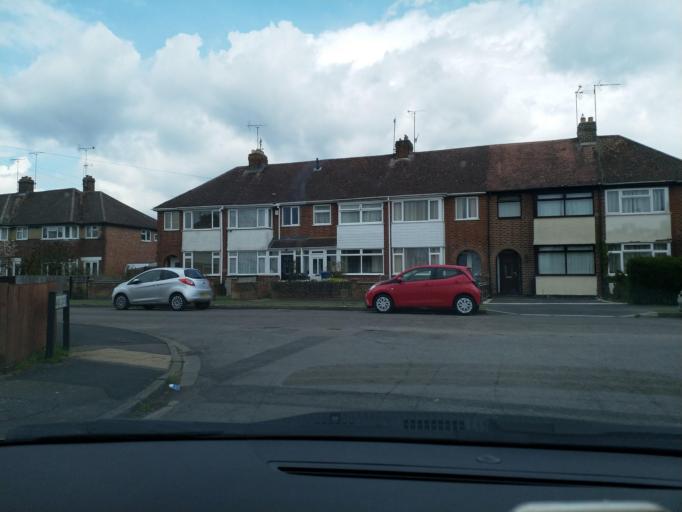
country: GB
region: England
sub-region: Suffolk
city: Woodbridge
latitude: 52.0689
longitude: 1.3250
